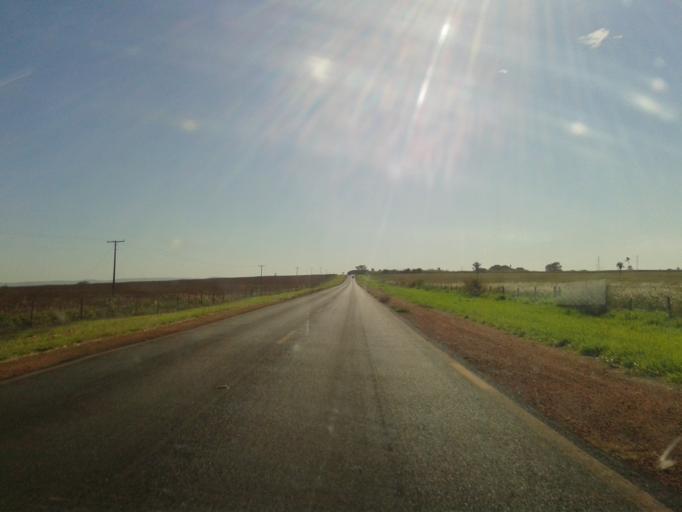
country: BR
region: Minas Gerais
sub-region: Capinopolis
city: Capinopolis
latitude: -18.5869
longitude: -49.5143
